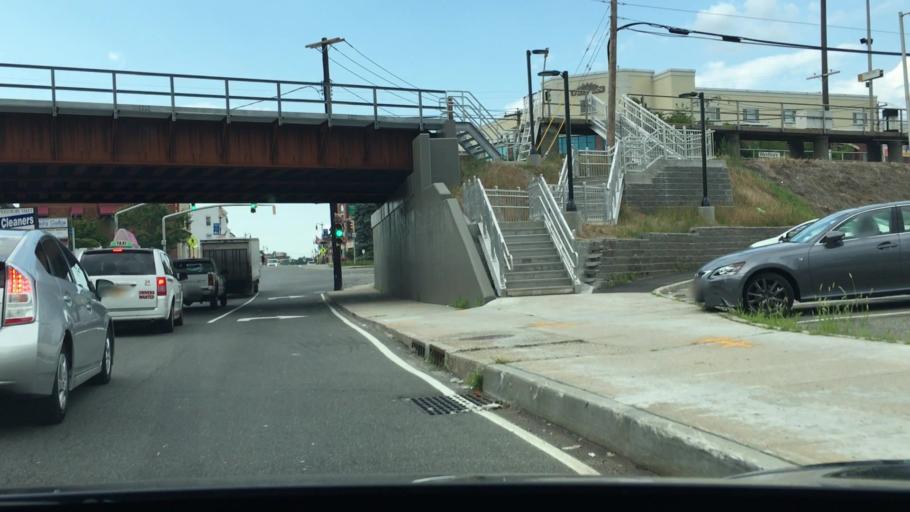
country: US
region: New York
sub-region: Nassau County
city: Westbury
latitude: 40.7527
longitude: -73.5877
